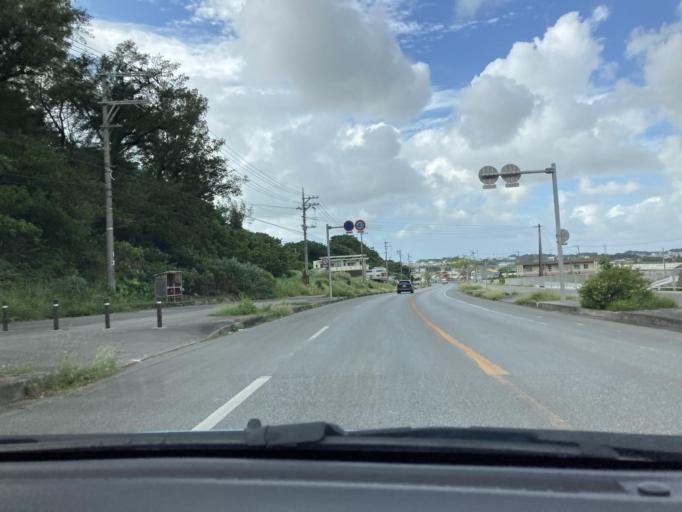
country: JP
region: Okinawa
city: Itoman
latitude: 26.1281
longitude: 127.6901
